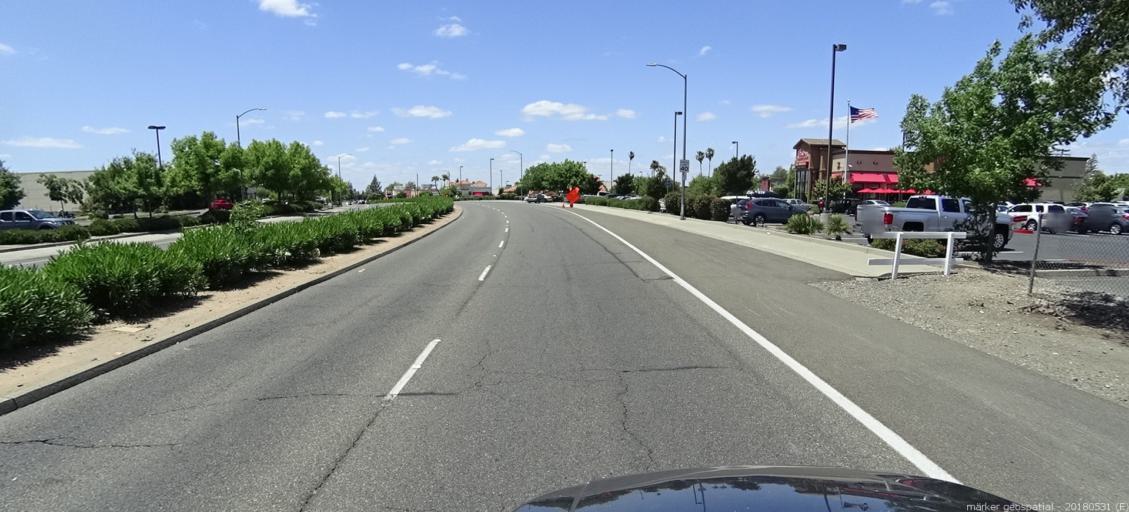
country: US
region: California
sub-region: Sacramento County
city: Arden-Arcade
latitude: 38.5984
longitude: -121.4167
